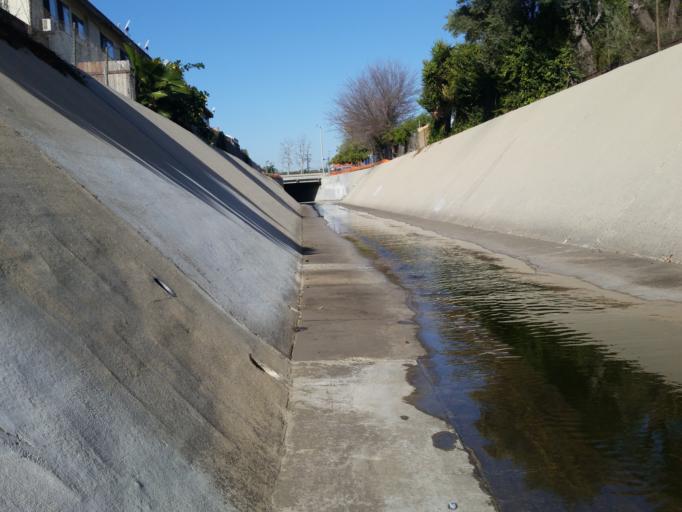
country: US
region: California
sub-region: Orange County
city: Buena Park
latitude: 33.8620
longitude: -117.9966
